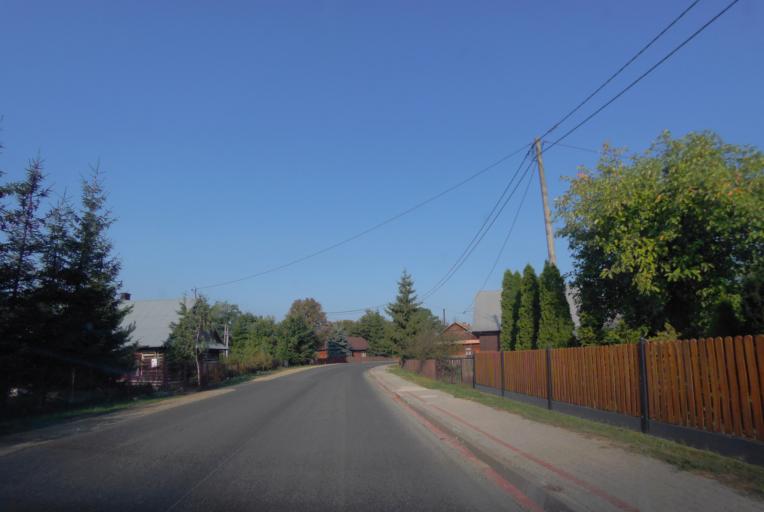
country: PL
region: Subcarpathian Voivodeship
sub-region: Powiat nizanski
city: Jarocin
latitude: 50.5095
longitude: 22.3590
